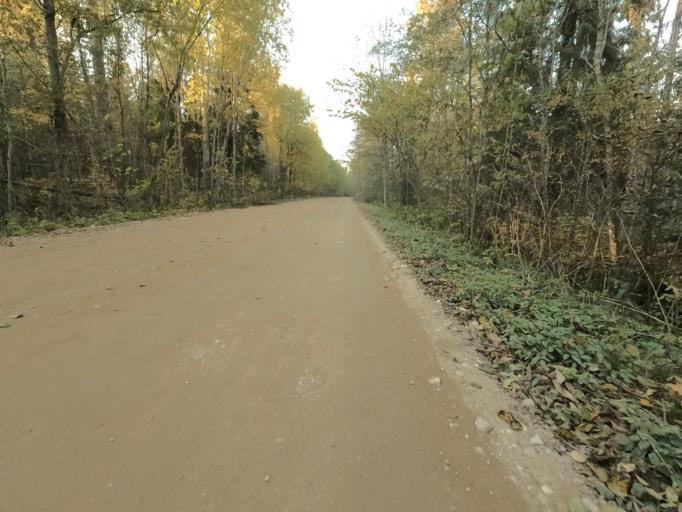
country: RU
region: Leningrad
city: Lyuban'
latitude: 58.9834
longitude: 31.0986
